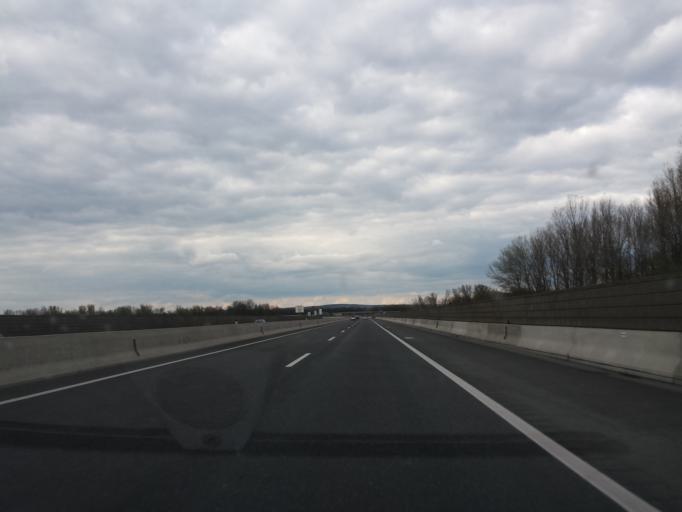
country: AT
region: Lower Austria
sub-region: Politischer Bezirk Krems
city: Grafenegg
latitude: 48.3982
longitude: 15.7351
